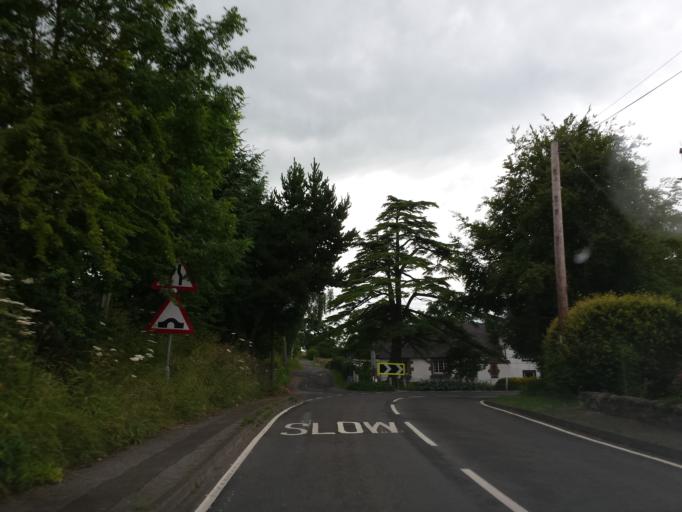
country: GB
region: Scotland
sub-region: Dumfries and Galloway
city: Dumfries
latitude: 55.0392
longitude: -3.6206
